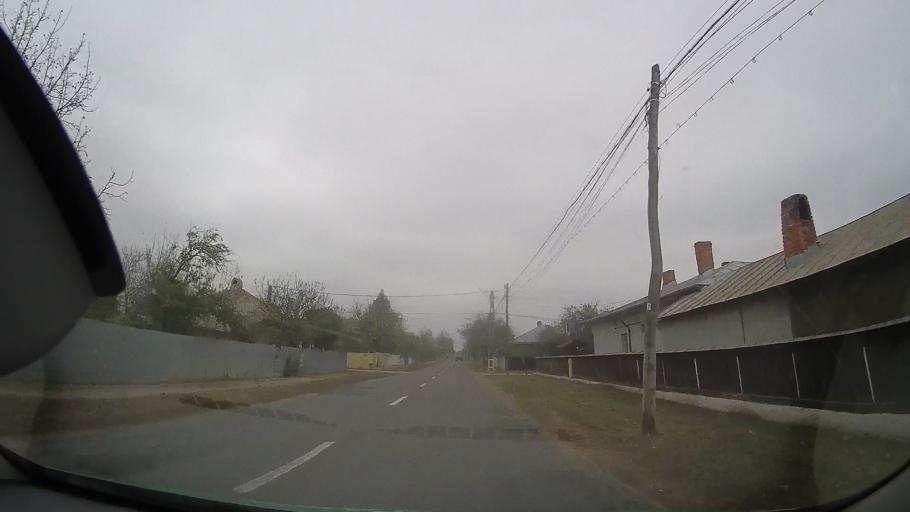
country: RO
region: Ialomita
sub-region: Comuna Grindu
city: Grindu
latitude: 44.7741
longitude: 26.9070
